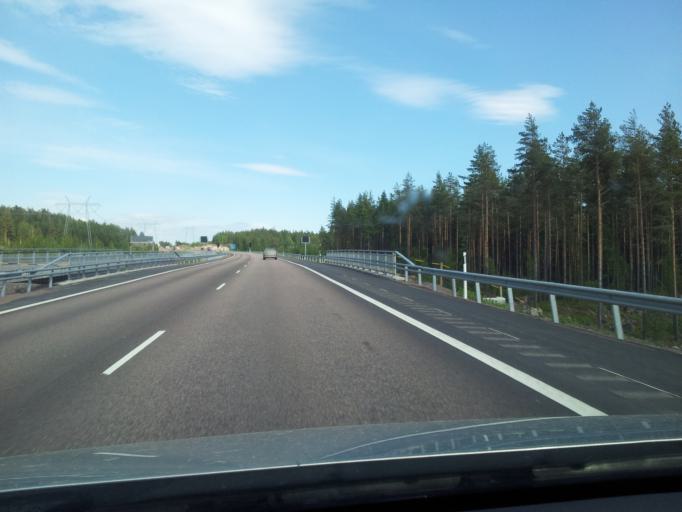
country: FI
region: Uusimaa
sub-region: Loviisa
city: Ruotsinpyhtaeae
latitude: 60.4872
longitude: 26.3886
